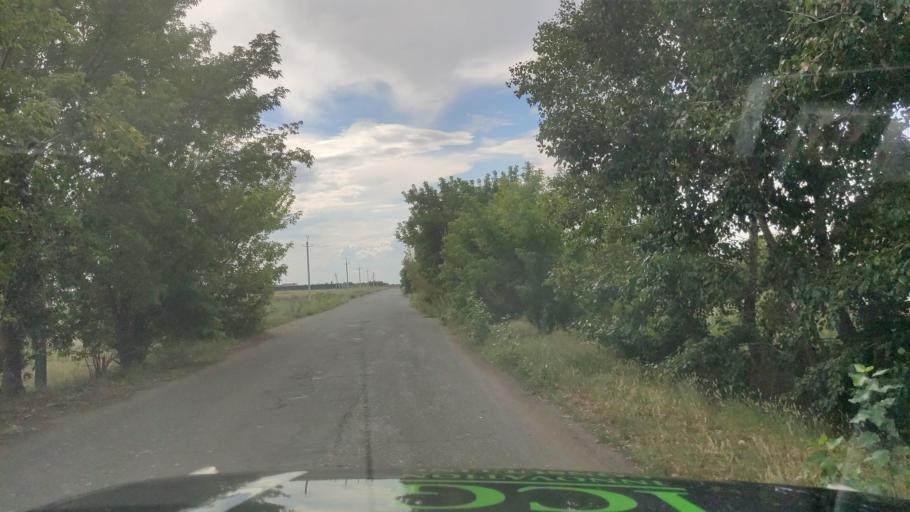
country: KZ
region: Pavlodar
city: Pavlodar
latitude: 52.6623
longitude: 77.5045
